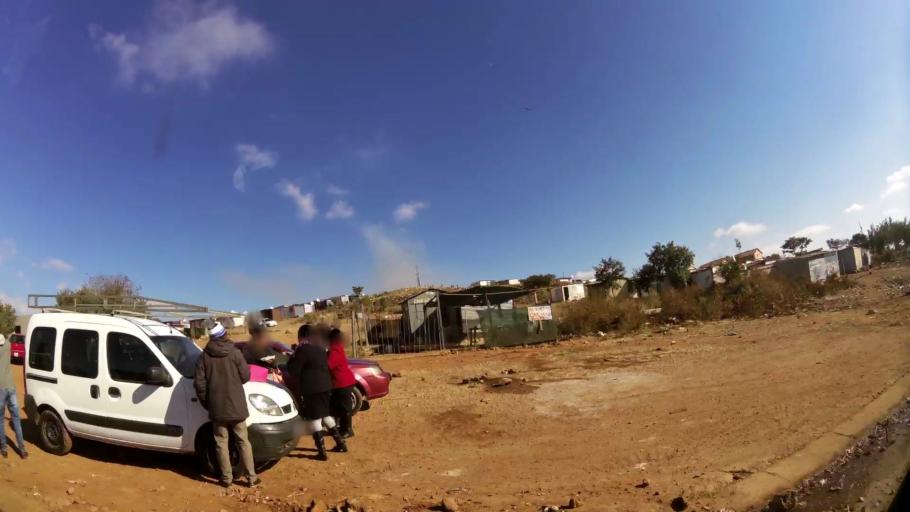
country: ZA
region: Gauteng
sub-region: City of Tshwane Metropolitan Municipality
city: Cullinan
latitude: -25.6943
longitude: 28.4167
